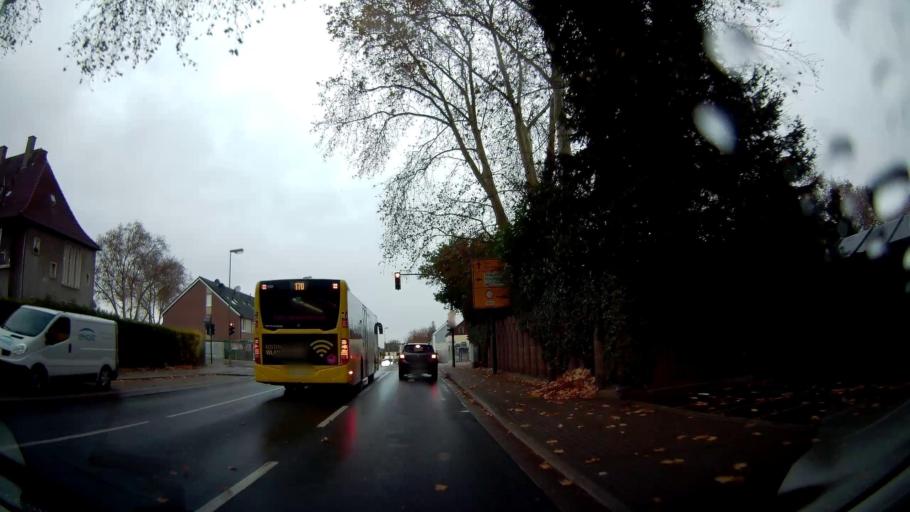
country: DE
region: North Rhine-Westphalia
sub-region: Regierungsbezirk Munster
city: Gelsenkirchen
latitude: 51.4746
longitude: 7.0810
